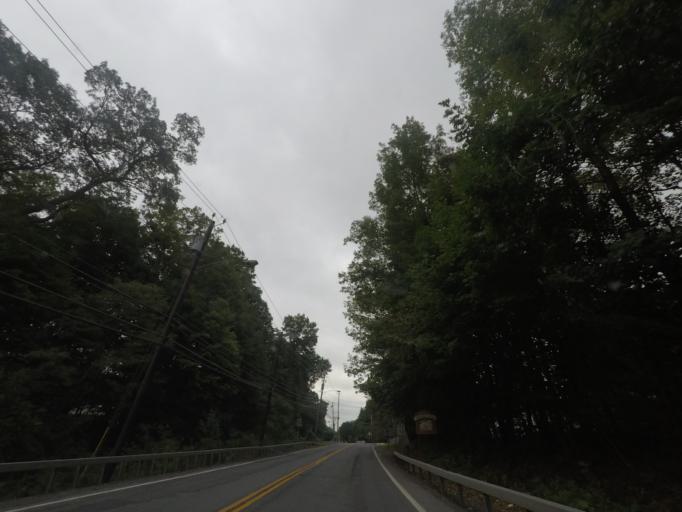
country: US
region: New York
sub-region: Rensselaer County
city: Hoosick Falls
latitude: 42.9104
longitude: -73.3516
